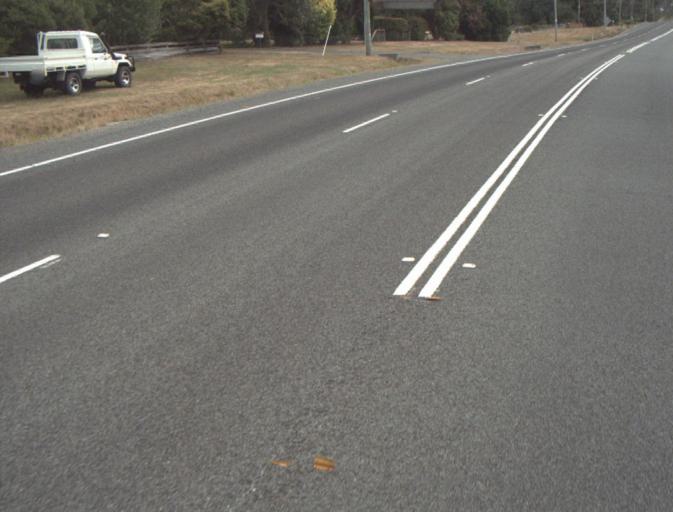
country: AU
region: Tasmania
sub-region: Launceston
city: Mayfield
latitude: -41.2861
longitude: 147.0405
